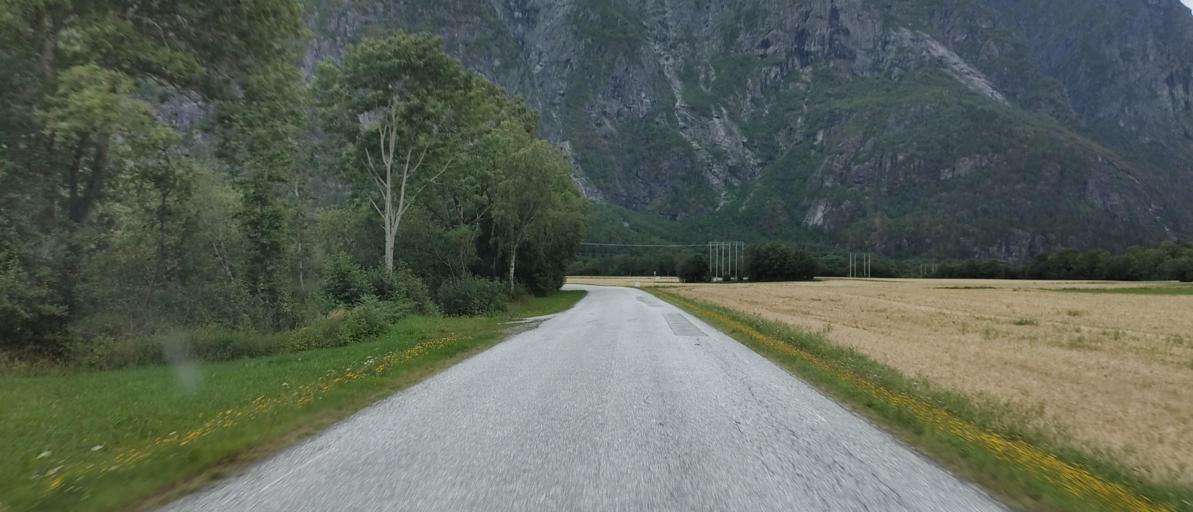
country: NO
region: More og Romsdal
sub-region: Rauma
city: Andalsnes
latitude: 62.5297
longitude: 7.7317
